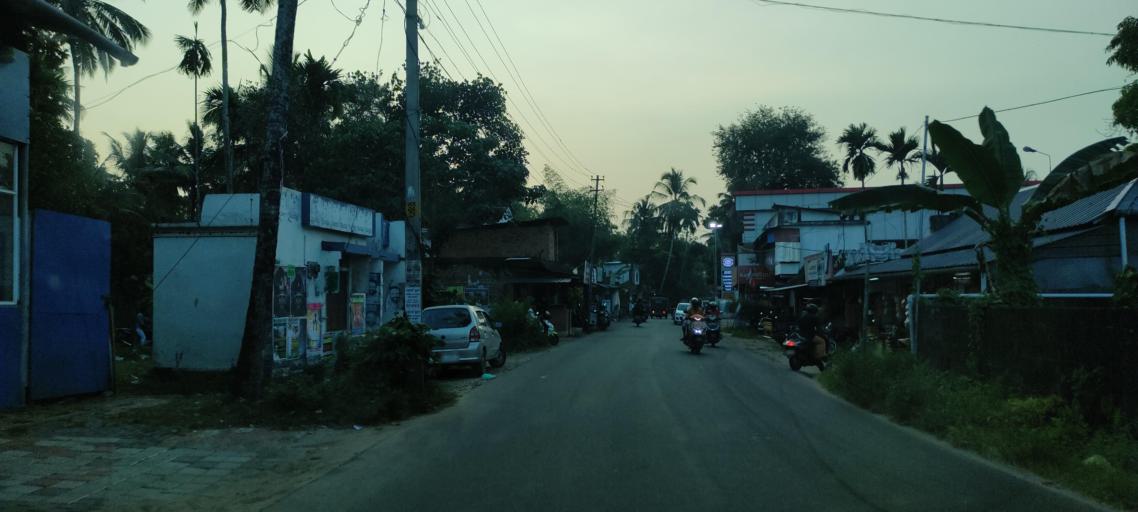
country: IN
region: Kerala
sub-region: Alappuzha
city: Kayankulam
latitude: 9.1336
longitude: 76.5090
